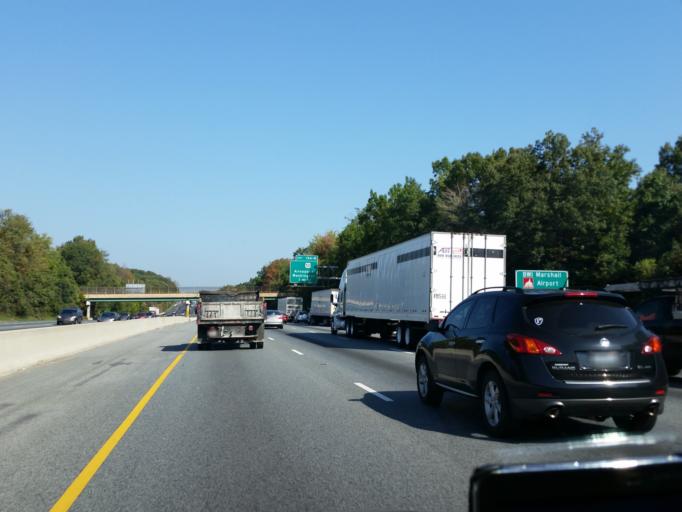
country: US
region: Maryland
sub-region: Prince George's County
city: Glenarden
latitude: 38.9288
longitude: -76.8543
